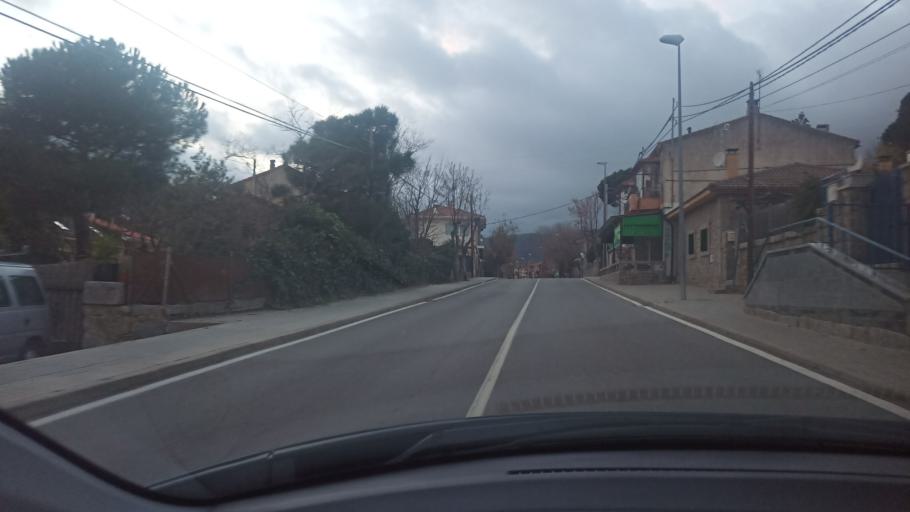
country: ES
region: Madrid
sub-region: Provincia de Madrid
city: Zarzalejo
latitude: 40.5396
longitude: -4.1599
